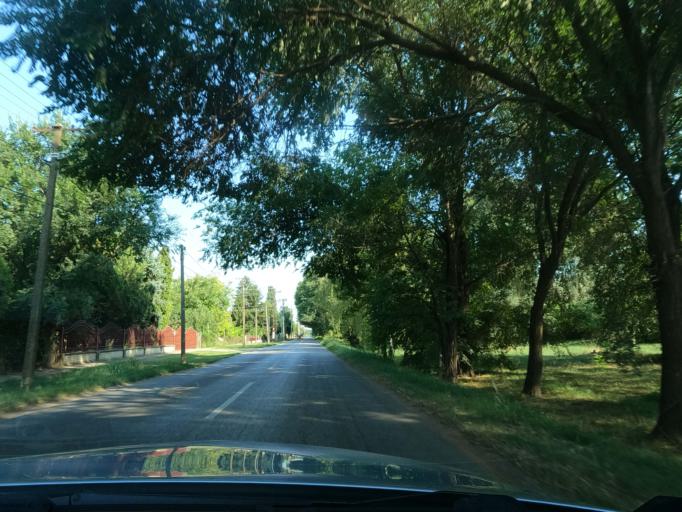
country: RS
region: Autonomna Pokrajina Vojvodina
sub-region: Juznobacki Okrug
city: Becej
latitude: 45.6299
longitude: 20.0189
